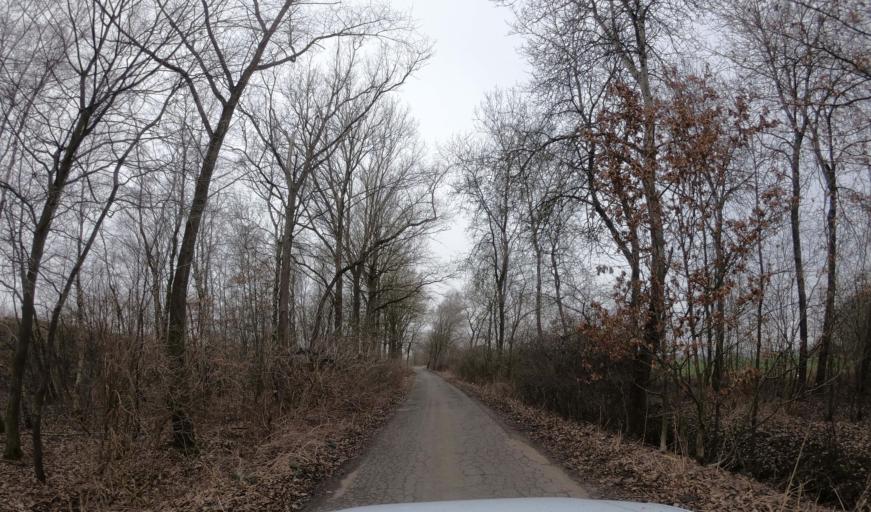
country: PL
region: West Pomeranian Voivodeship
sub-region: Powiat gryficki
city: Ploty
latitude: 53.8604
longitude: 15.2601
